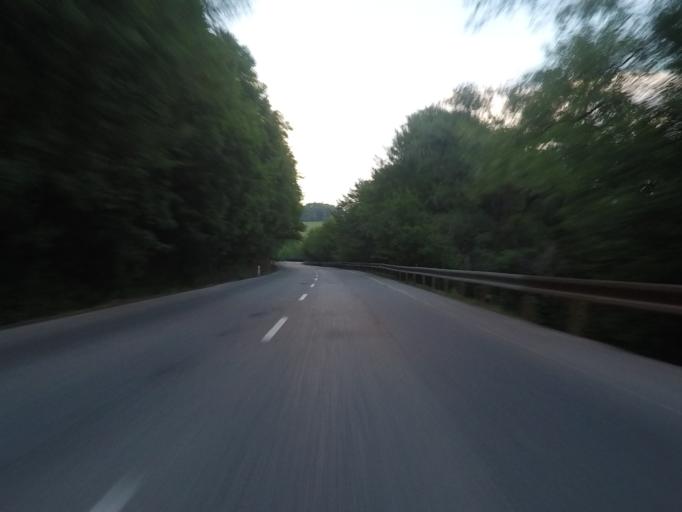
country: SK
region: Banskobystricky
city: Tisovec
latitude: 48.5217
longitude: 19.9451
